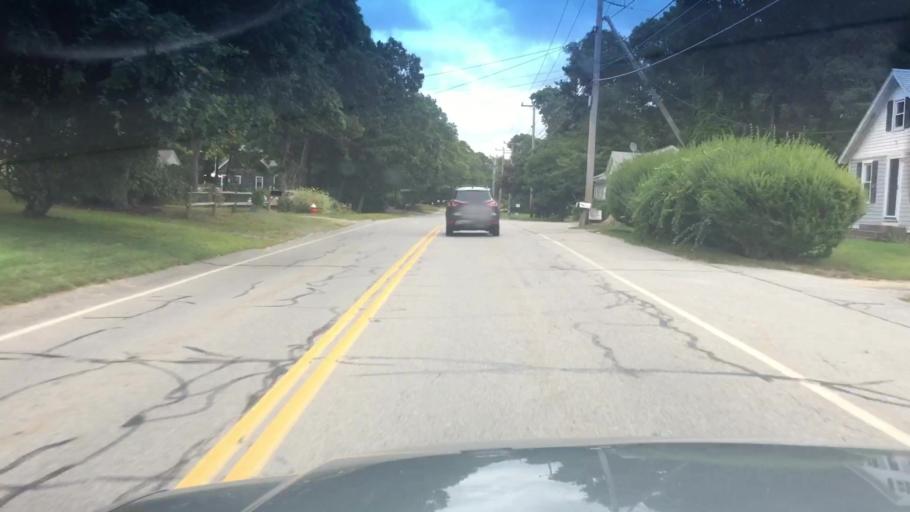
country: US
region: Massachusetts
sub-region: Barnstable County
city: Pocasset
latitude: 41.6959
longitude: -70.6029
